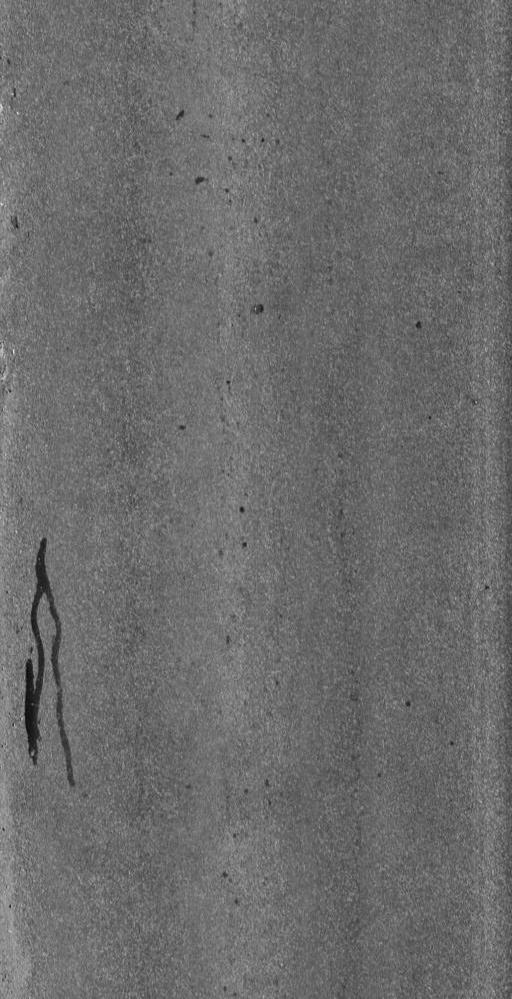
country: US
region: Vermont
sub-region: Chittenden County
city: Burlington
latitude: 44.4701
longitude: -73.2004
